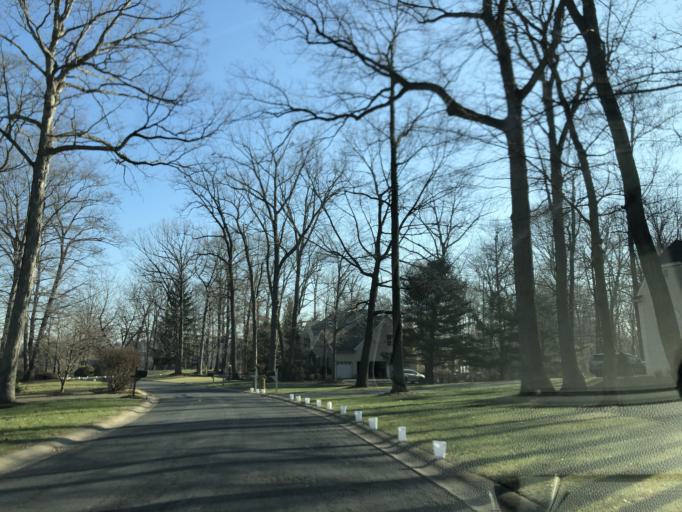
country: US
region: Pennsylvania
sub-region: Chester County
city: Downingtown
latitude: 39.9870
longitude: -75.6970
